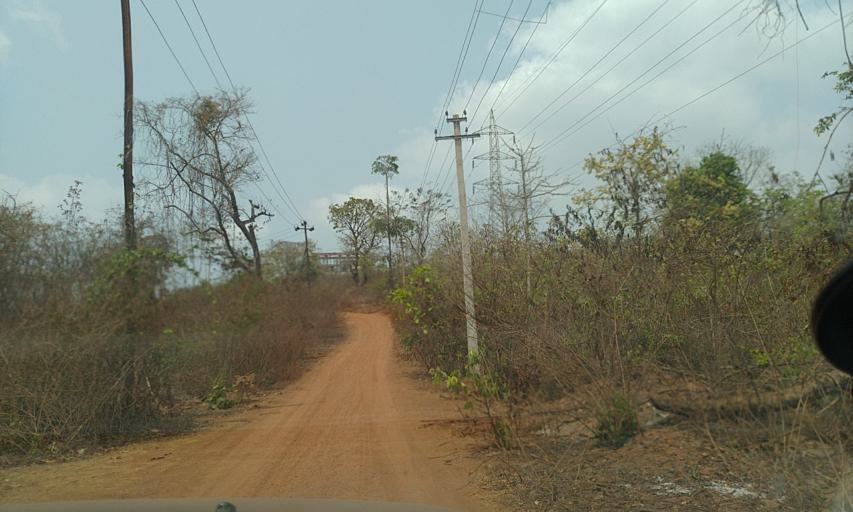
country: IN
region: Goa
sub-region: North Goa
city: Goa Velha
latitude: 15.4849
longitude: 73.9139
